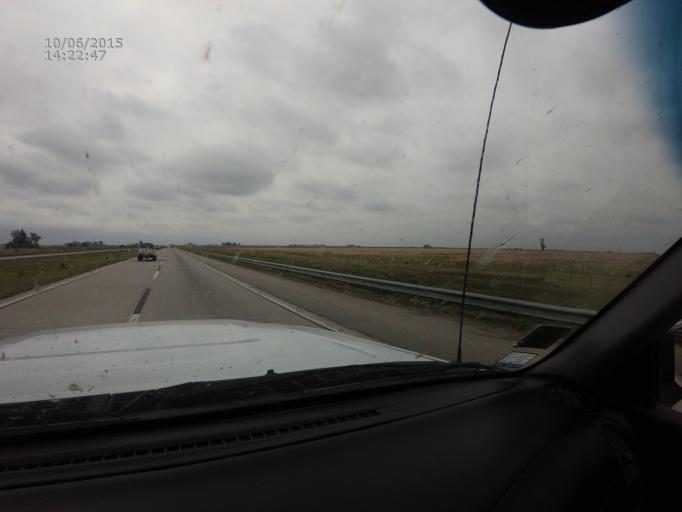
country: AR
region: Cordoba
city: Tio Pujio
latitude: -32.3078
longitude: -63.2833
